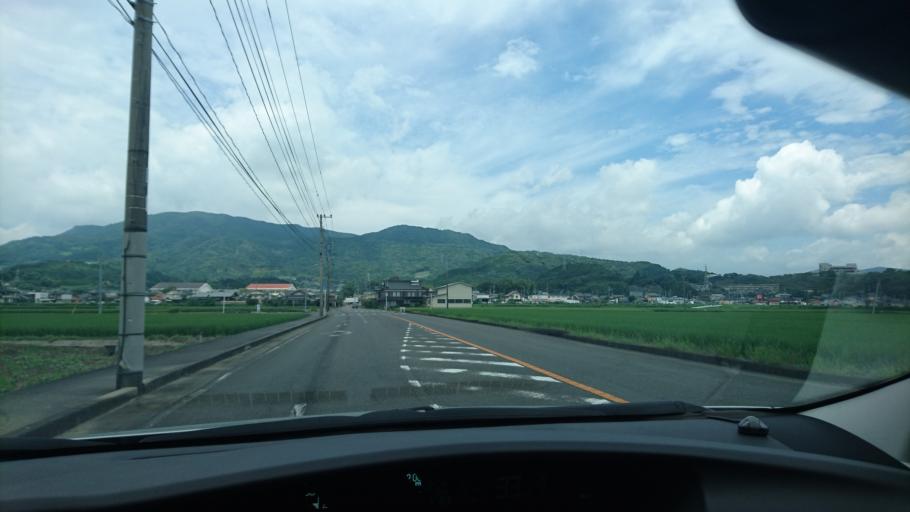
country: JP
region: Saga Prefecture
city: Takeocho-takeo
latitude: 33.2095
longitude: 130.1213
